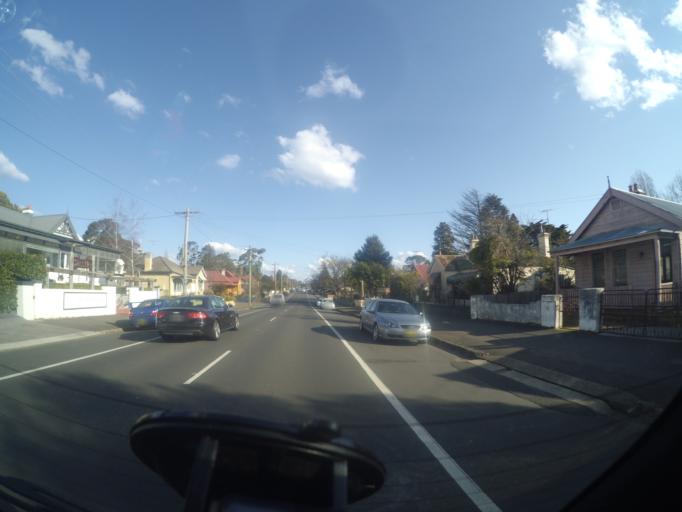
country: AU
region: New South Wales
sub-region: Blue Mountains Municipality
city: Katoomba
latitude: -33.7202
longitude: 150.3119
